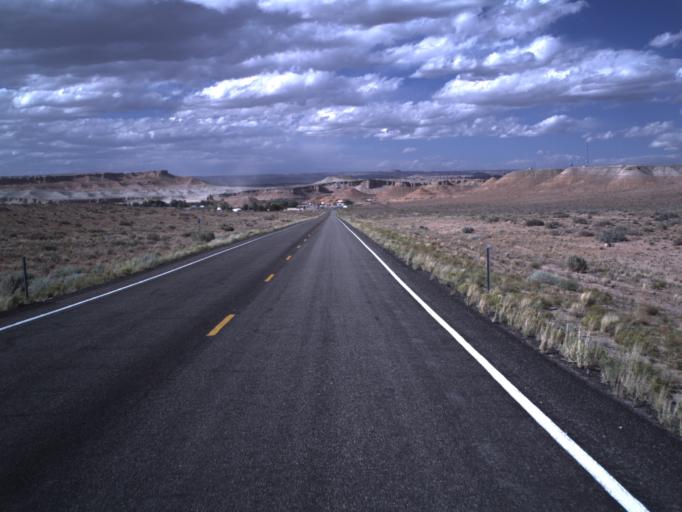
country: US
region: Utah
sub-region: Emery County
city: Ferron
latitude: 38.3597
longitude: -110.6987
